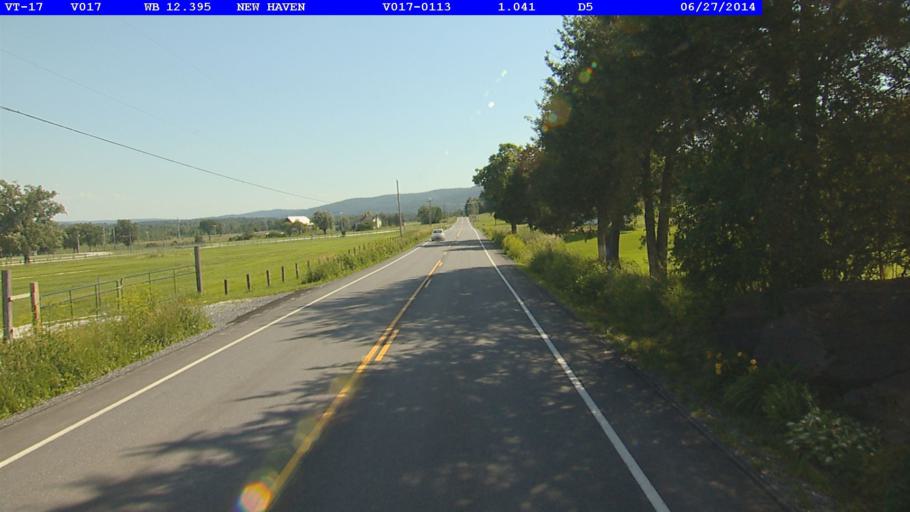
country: US
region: Vermont
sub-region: Addison County
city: Vergennes
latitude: 44.0944
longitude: -73.2309
